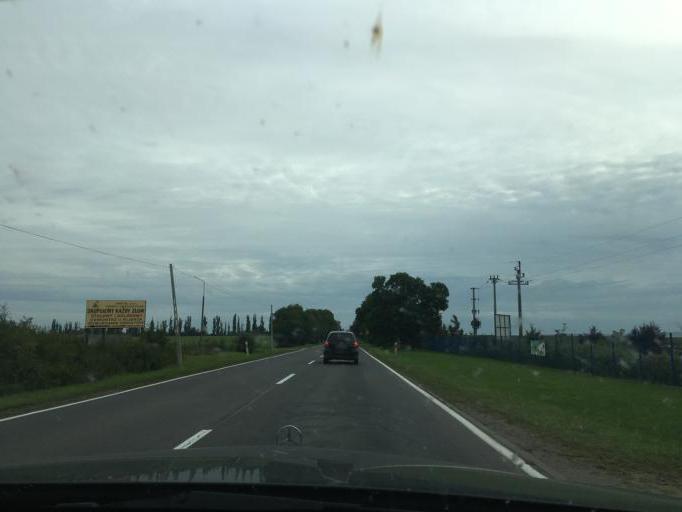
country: PL
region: Masovian Voivodeship
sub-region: Powiat ostrowski
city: Ostrow Mazowiecka
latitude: 52.8488
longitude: 21.8683
